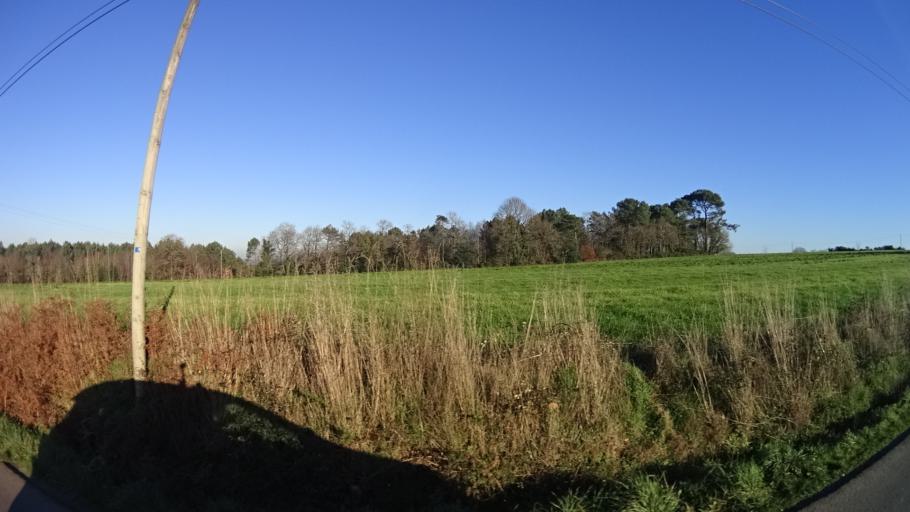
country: FR
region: Brittany
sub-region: Departement du Morbihan
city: Allaire
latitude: 47.6593
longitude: -2.1749
